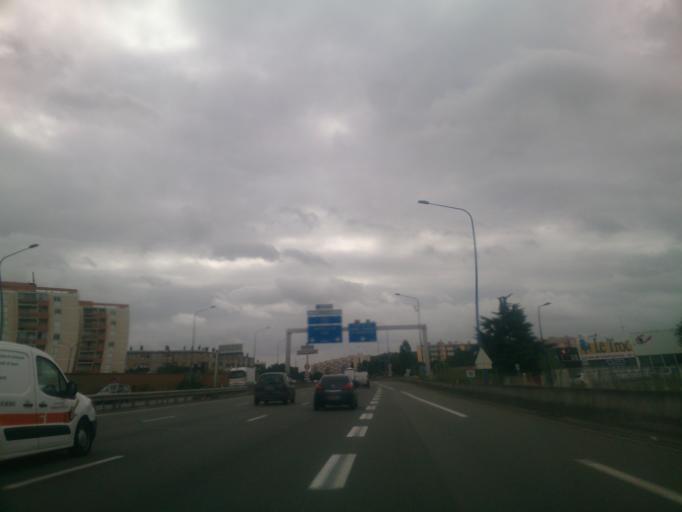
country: FR
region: Midi-Pyrenees
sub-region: Departement de la Haute-Garonne
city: Toulouse
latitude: 43.5739
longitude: 1.4097
